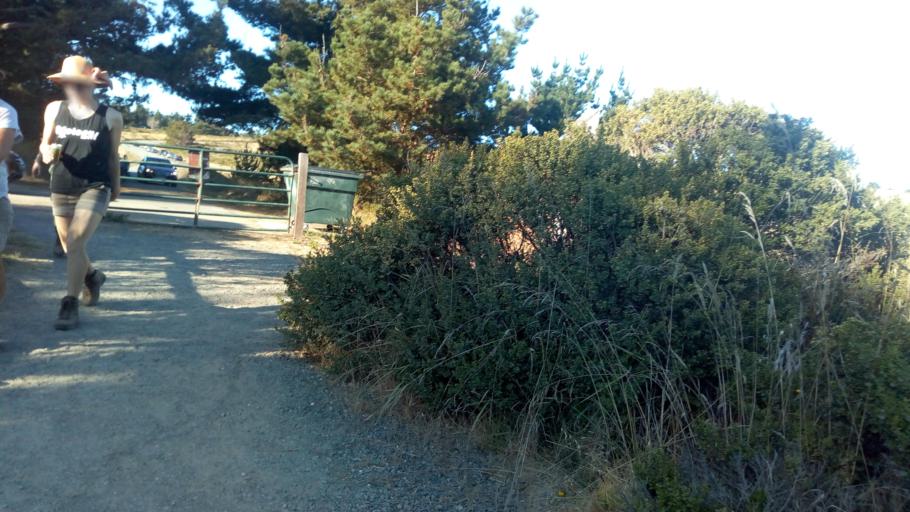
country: US
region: California
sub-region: Marin County
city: Inverness
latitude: 38.0280
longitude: -122.8824
